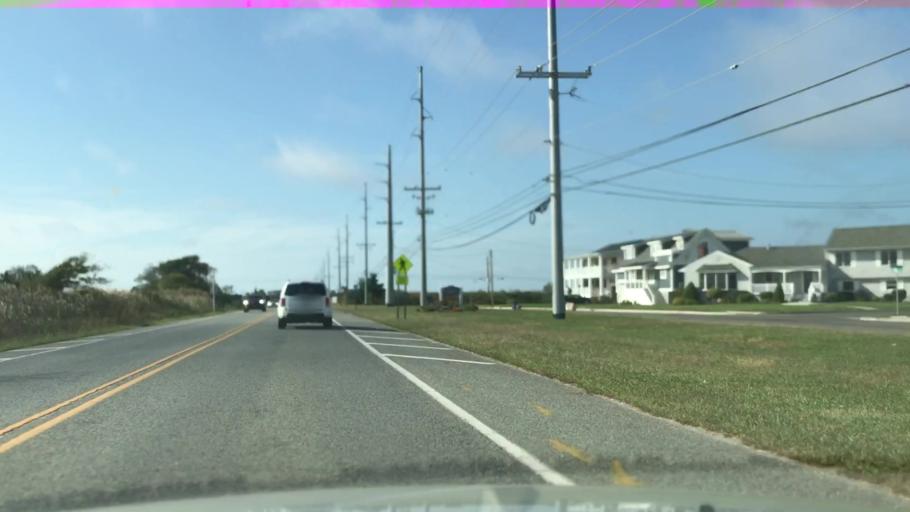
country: US
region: New Jersey
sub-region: Cape May County
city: Cape May Court House
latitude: 39.0602
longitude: -74.7708
